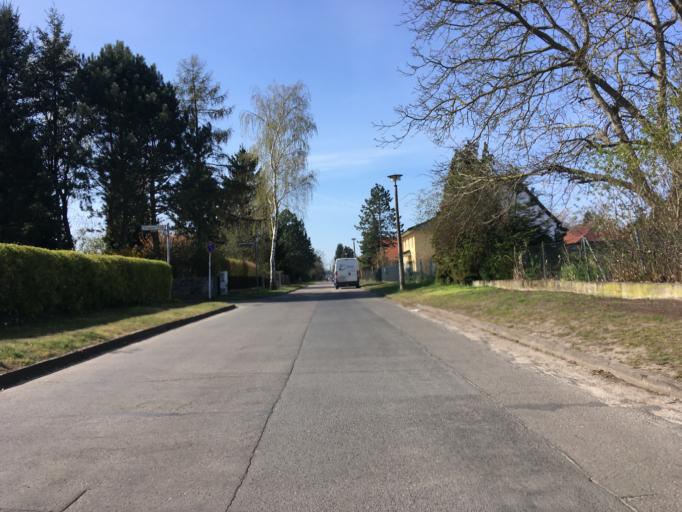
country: DE
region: Berlin
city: Kaulsdorf
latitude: 52.4990
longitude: 13.5860
